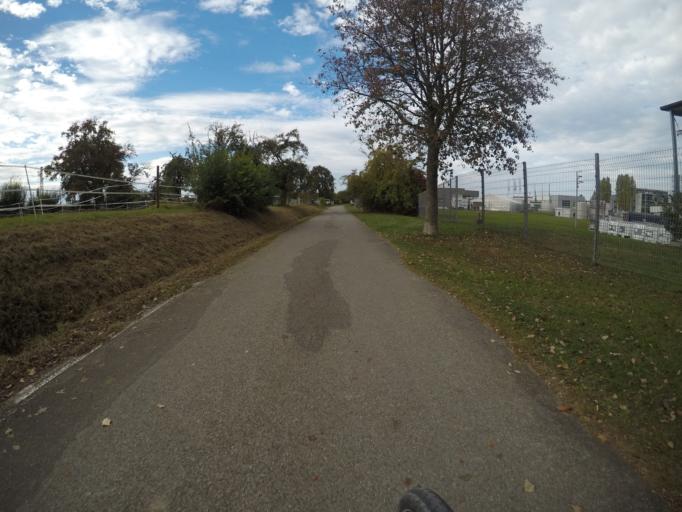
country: DE
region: Baden-Wuerttemberg
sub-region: Regierungsbezirk Stuttgart
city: Herrenberg
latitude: 48.6015
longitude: 8.8661
